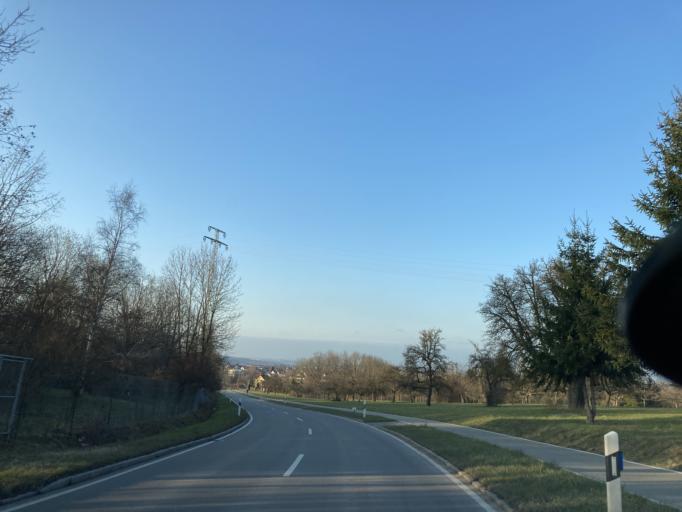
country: DE
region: Baden-Wuerttemberg
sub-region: Tuebingen Region
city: Nehren
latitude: 48.4190
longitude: 9.0669
